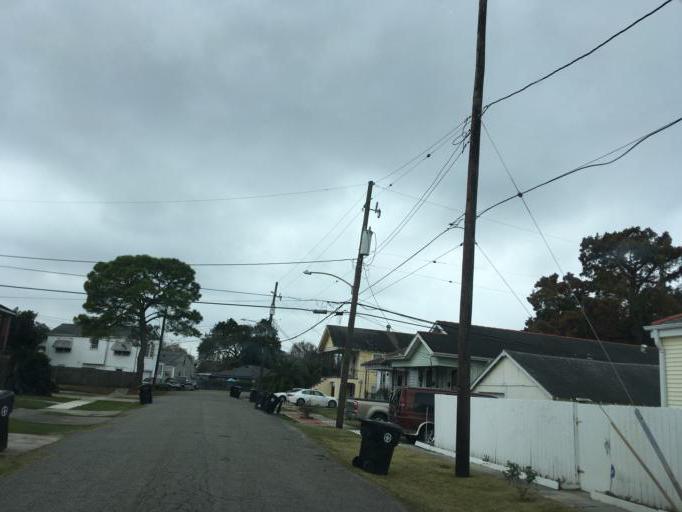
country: US
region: Louisiana
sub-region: Orleans Parish
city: New Orleans
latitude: 29.9954
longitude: -90.0556
